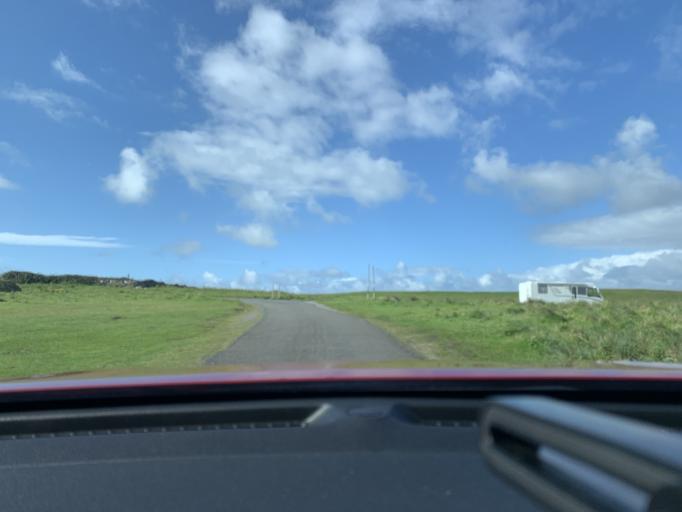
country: IE
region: Connaught
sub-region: Sligo
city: Strandhill
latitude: 54.3978
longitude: -8.5662
